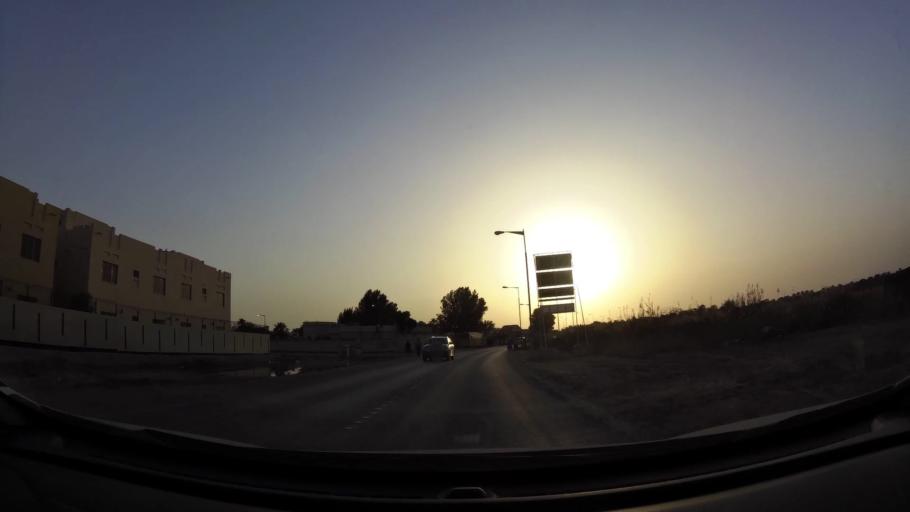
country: BH
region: Central Governorate
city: Madinat Hamad
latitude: 26.1824
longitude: 50.4684
